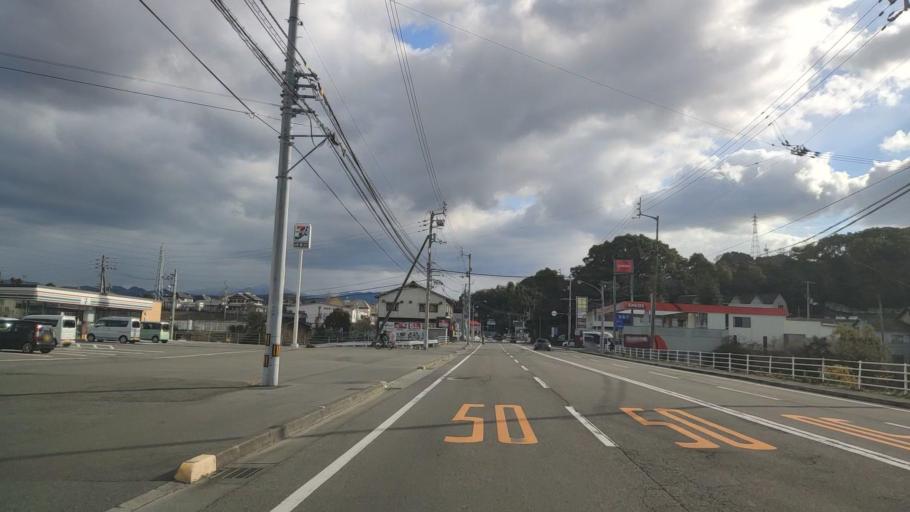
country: JP
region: Ehime
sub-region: Shikoku-chuo Shi
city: Matsuyama
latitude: 33.8564
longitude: 132.7313
